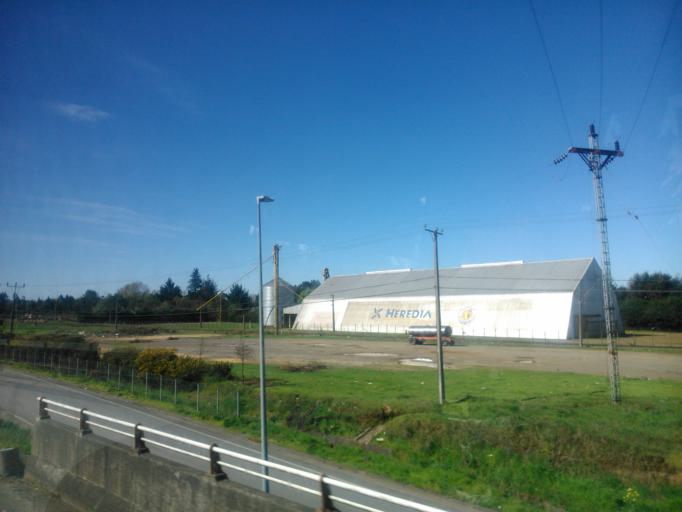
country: CL
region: Araucania
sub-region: Provincia de Cautin
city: Temuco
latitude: -38.8325
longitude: -72.6237
